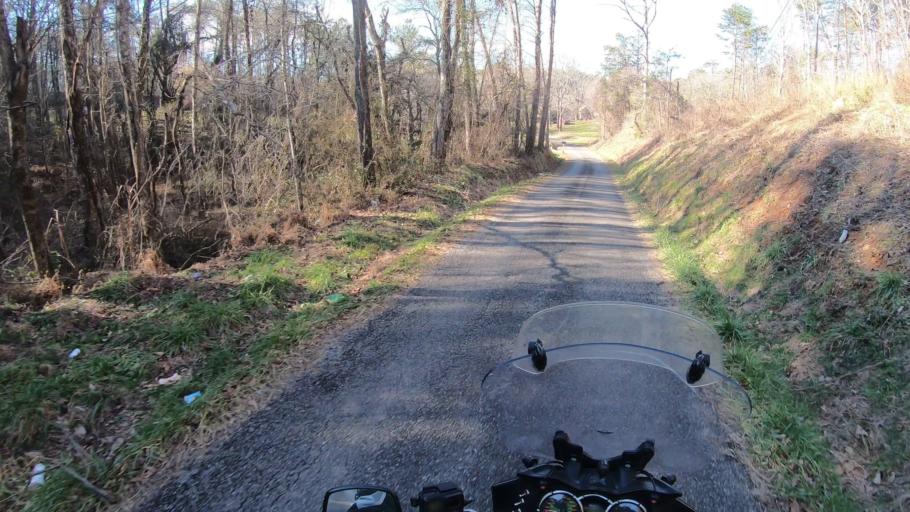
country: US
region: Georgia
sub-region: Fannin County
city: McCaysville
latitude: 34.9975
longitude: -84.3272
